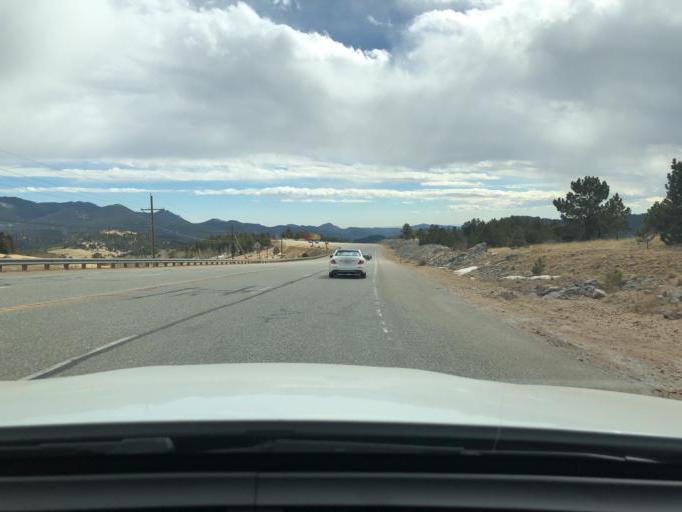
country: US
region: Colorado
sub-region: Gilpin County
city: Central City
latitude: 39.7904
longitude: -105.5081
